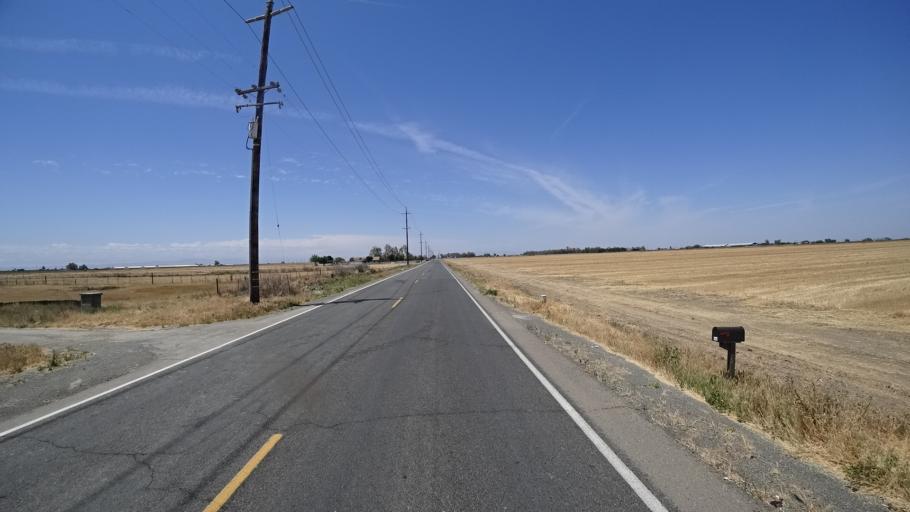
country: US
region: California
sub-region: Kings County
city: Lemoore
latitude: 36.2403
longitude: -119.7875
